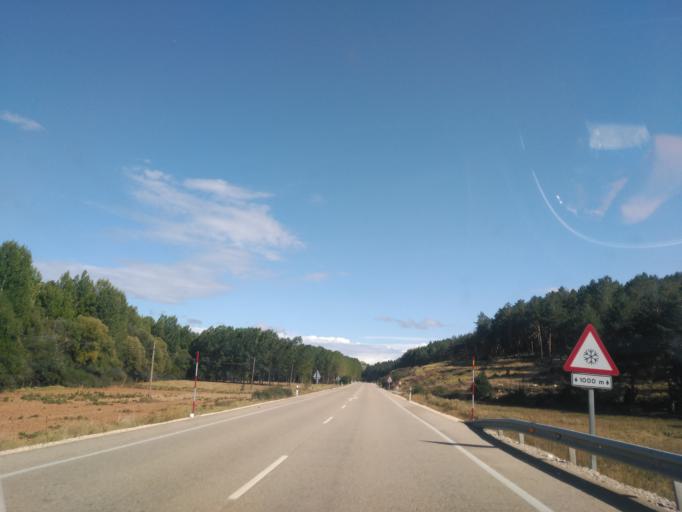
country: ES
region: Castille and Leon
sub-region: Provincia de Burgos
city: Rabanera del Pinar
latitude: 41.8655
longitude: -3.2085
